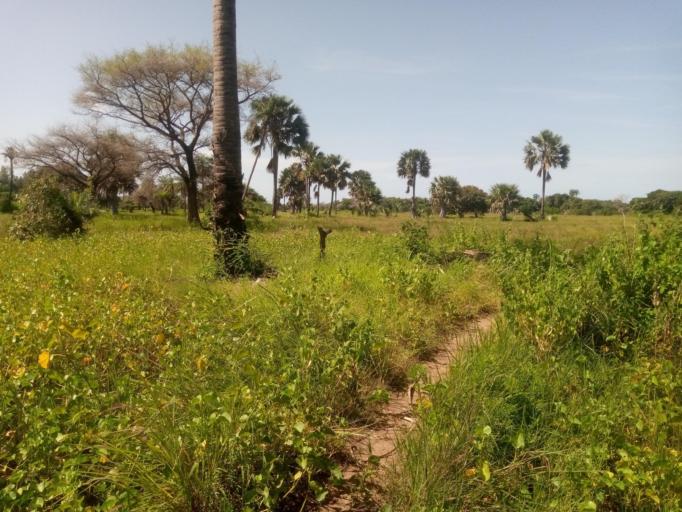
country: GM
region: Western
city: Gunjur
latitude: 13.0380
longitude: -16.7302
